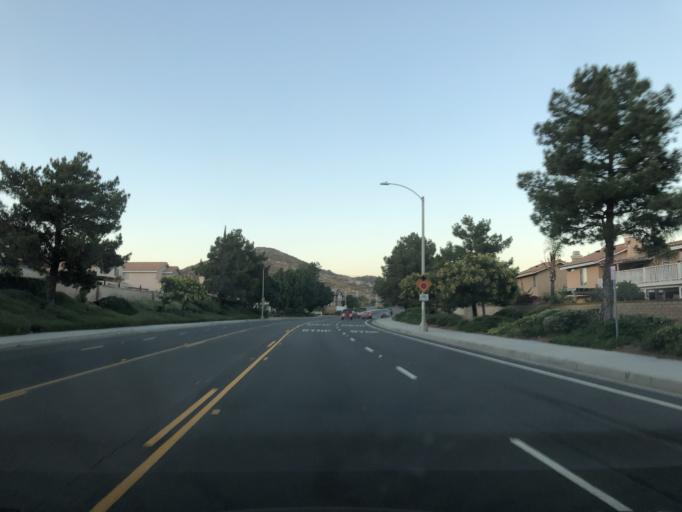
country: US
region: California
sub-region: Riverside County
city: Home Gardens
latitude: 33.8993
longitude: -117.5077
